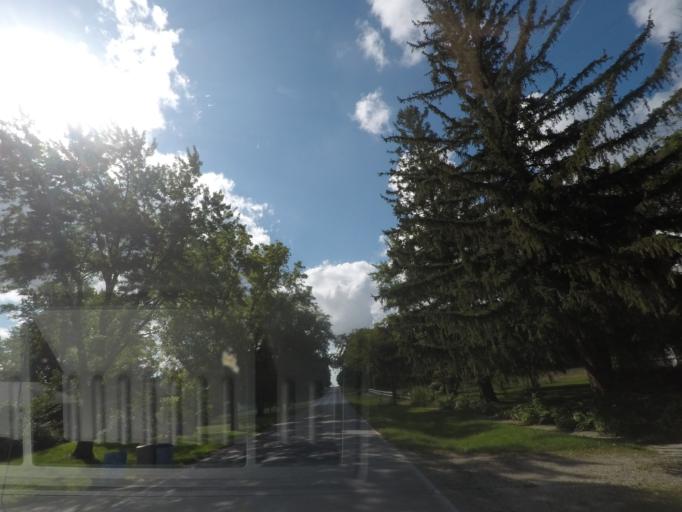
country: US
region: Iowa
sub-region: Story County
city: Nevada
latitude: 42.0161
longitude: -93.3192
